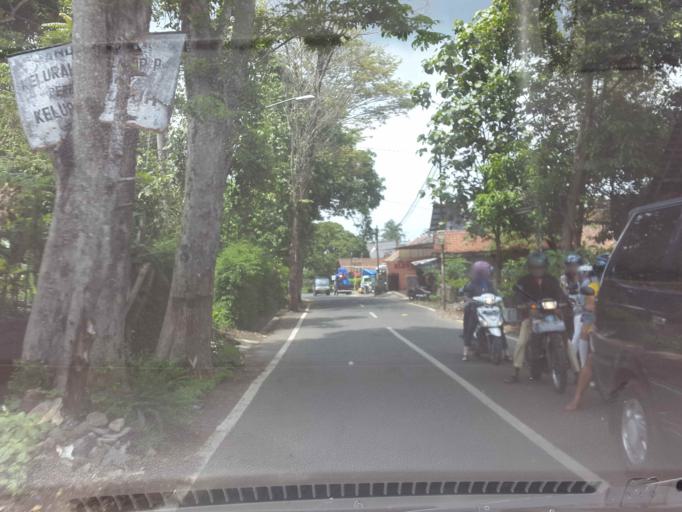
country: ID
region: Central Java
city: Salatiga
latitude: -7.3422
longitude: 110.4938
